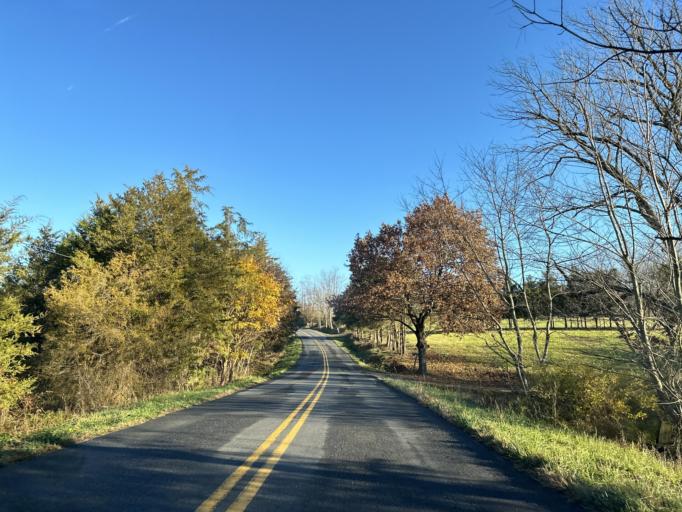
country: US
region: Virginia
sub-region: Rockingham County
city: Bridgewater
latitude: 38.3222
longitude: -78.9860
